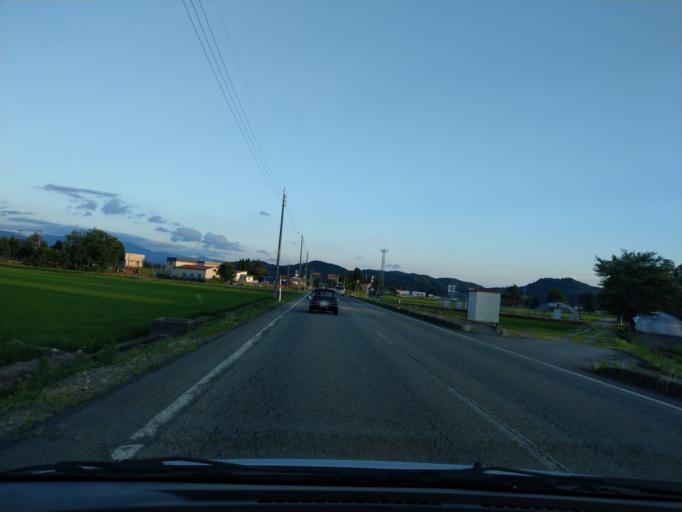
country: JP
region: Akita
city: Kakunodatemachi
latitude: 39.6252
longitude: 140.5716
